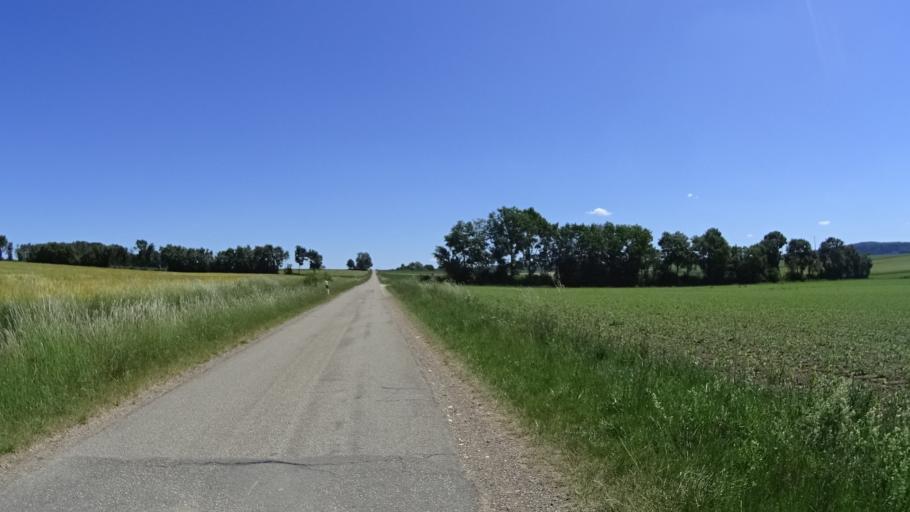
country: DE
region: Bavaria
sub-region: Regierungsbezirk Mittelfranken
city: Hottingen
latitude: 49.0818
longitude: 11.0043
